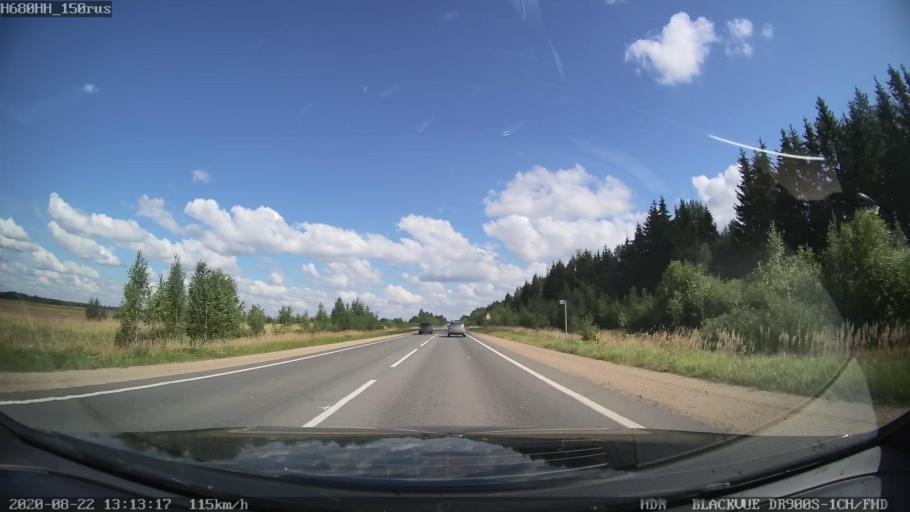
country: RU
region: Tverskaya
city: Bezhetsk
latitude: 57.7491
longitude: 36.5690
